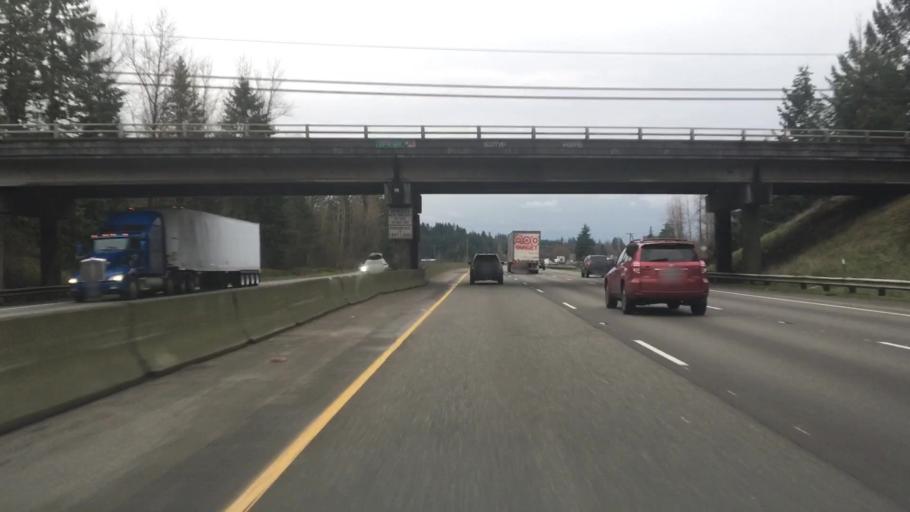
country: US
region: Washington
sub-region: Thurston County
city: Tumwater
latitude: 46.9239
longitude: -122.9460
